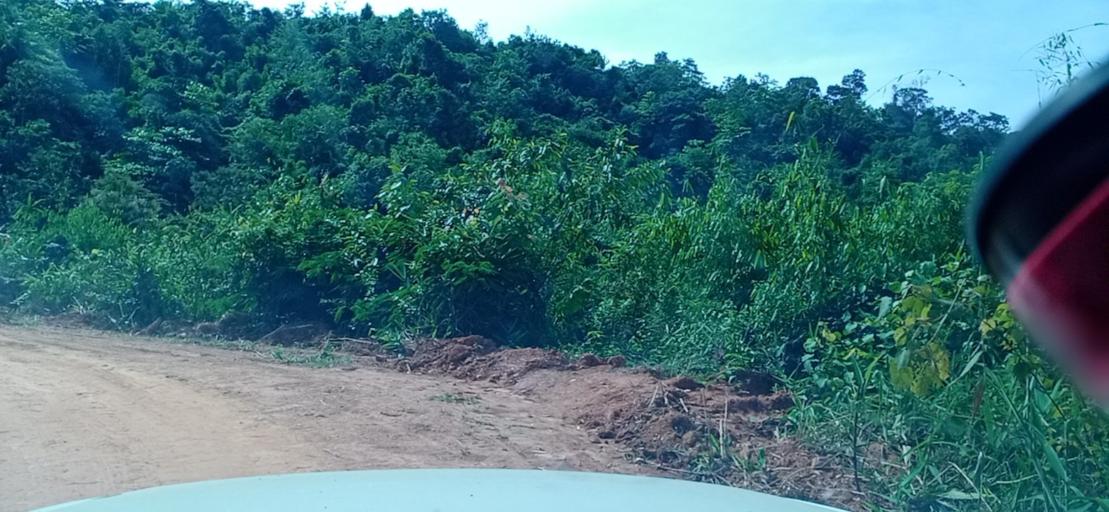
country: TH
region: Changwat Bueng Kan
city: Pak Khat
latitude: 18.6343
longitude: 103.2605
